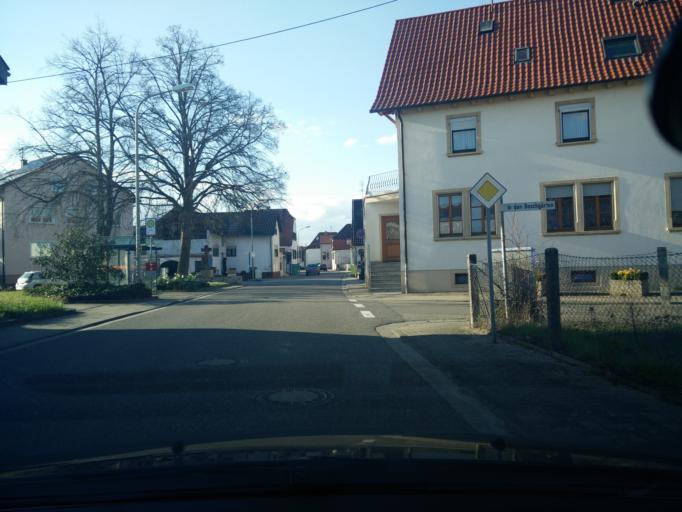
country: DE
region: Rheinland-Pfalz
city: Vollmersweiler
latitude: 49.0560
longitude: 8.0860
